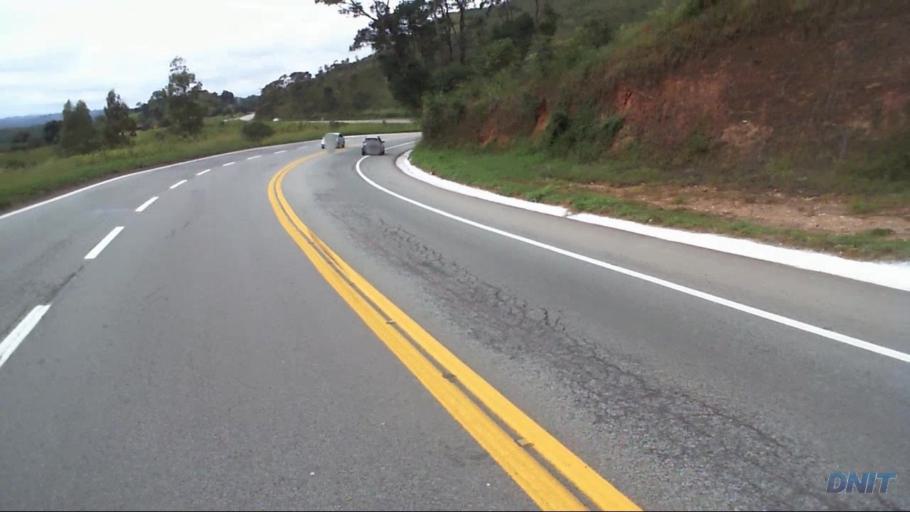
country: BR
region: Minas Gerais
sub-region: Caete
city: Caete
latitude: -19.7875
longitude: -43.6924
